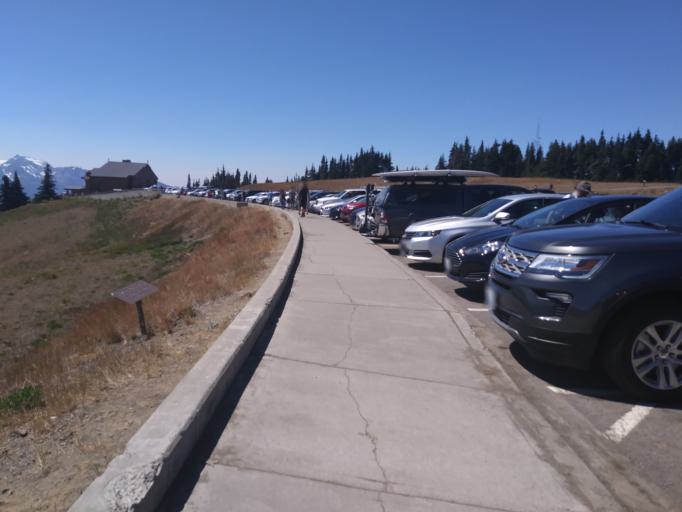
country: US
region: Washington
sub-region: Clallam County
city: Port Angeles
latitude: 47.9700
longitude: -123.4963
